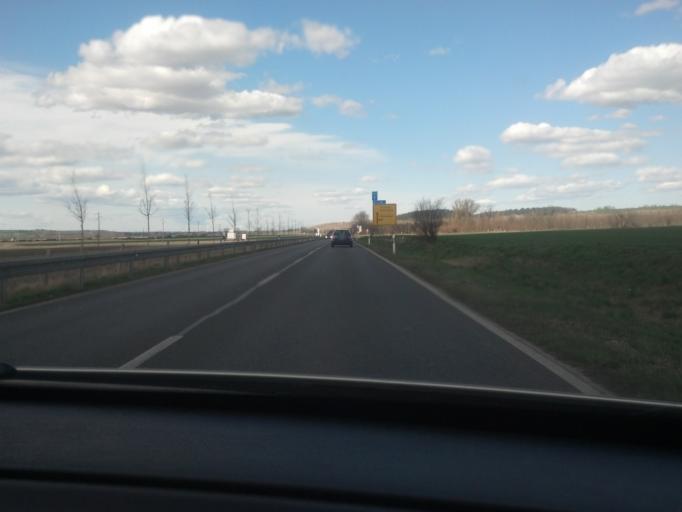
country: DE
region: Mecklenburg-Vorpommern
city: Trollenhagen
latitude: 53.5990
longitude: 13.2710
